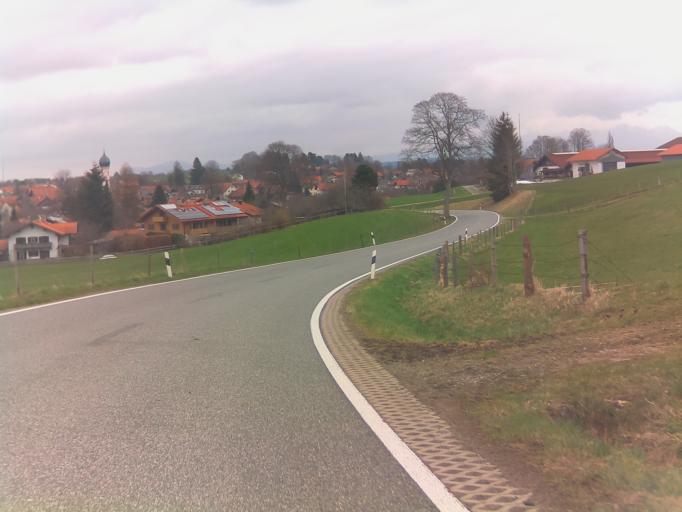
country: DE
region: Bavaria
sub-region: Upper Bavaria
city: Uffing
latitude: 47.7143
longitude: 11.1400
